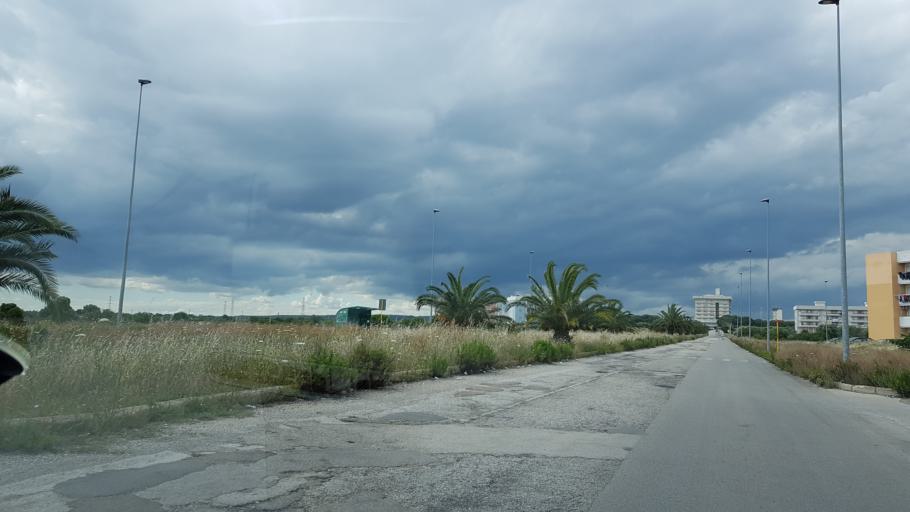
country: IT
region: Apulia
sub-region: Provincia di Taranto
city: Paolo VI
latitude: 40.5319
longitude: 17.2770
